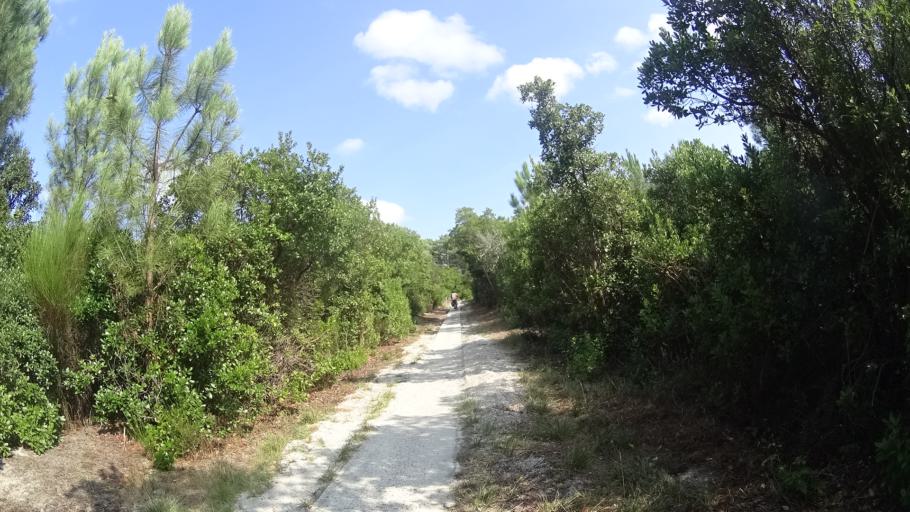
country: FR
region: Aquitaine
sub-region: Departement de la Gironde
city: Lacanau
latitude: 44.9651
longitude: -1.1751
